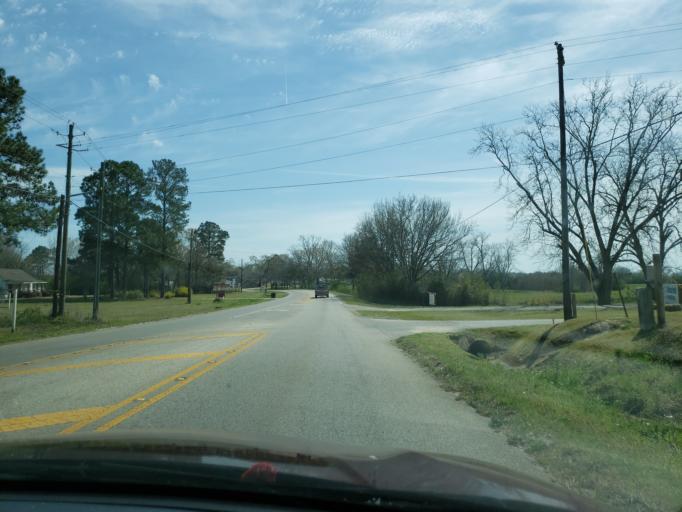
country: US
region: Alabama
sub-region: Elmore County
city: Tallassee
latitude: 32.5696
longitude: -85.9381
